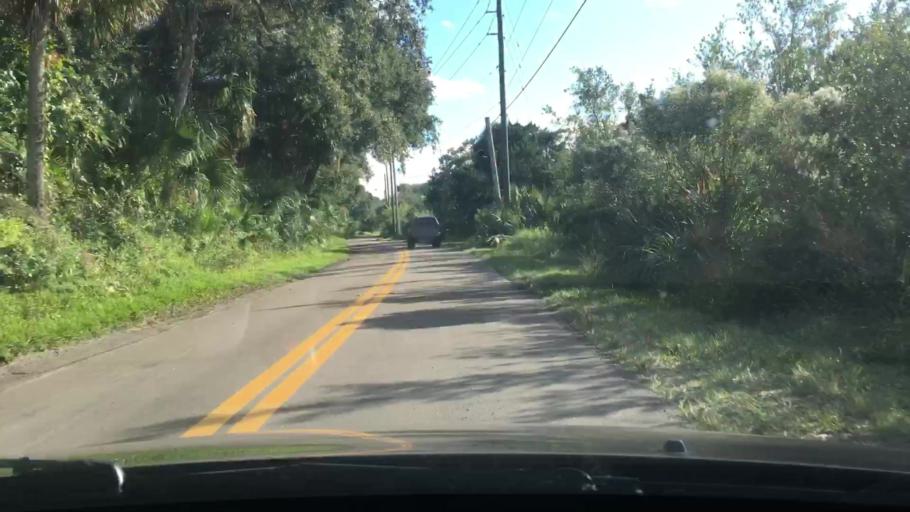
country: US
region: Florida
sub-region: Volusia County
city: Ormond-by-the-Sea
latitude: 29.3902
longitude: -81.0900
